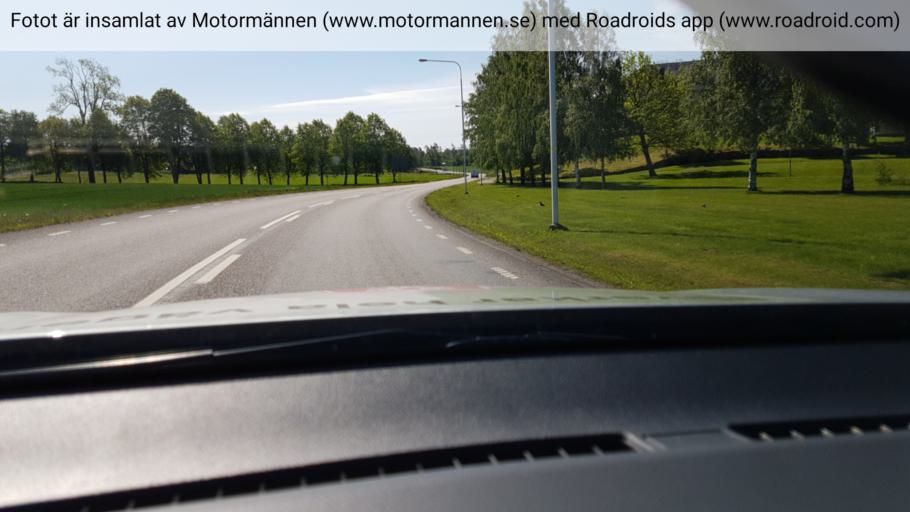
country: SE
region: Vaestra Goetaland
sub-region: Tibro Kommun
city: Tibro
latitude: 58.4097
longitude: 14.1841
